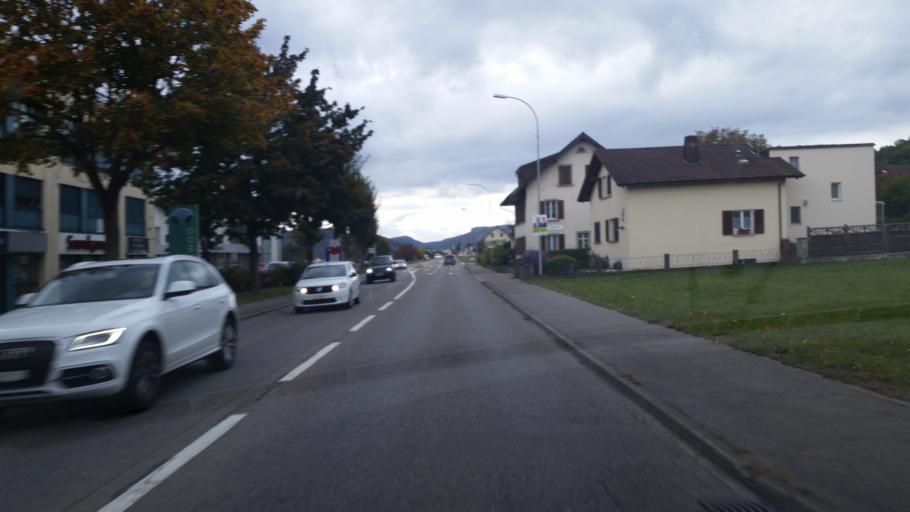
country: CH
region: Aargau
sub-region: Bezirk Baden
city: Turgi
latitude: 47.4936
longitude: 8.2757
